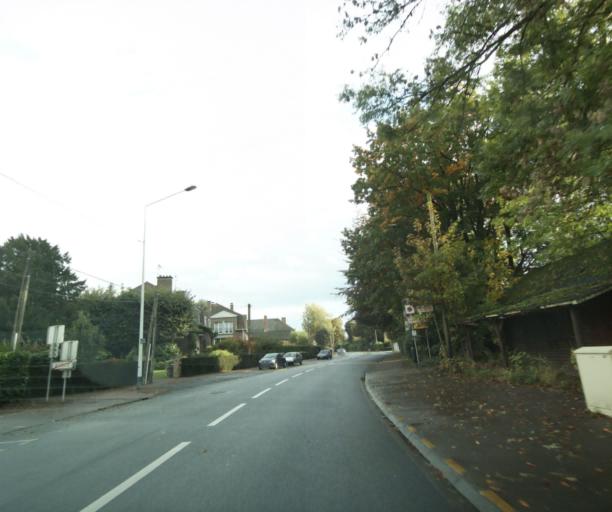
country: FR
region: Nord-Pas-de-Calais
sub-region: Departement du Nord
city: Roncq
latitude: 50.7344
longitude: 3.1299
